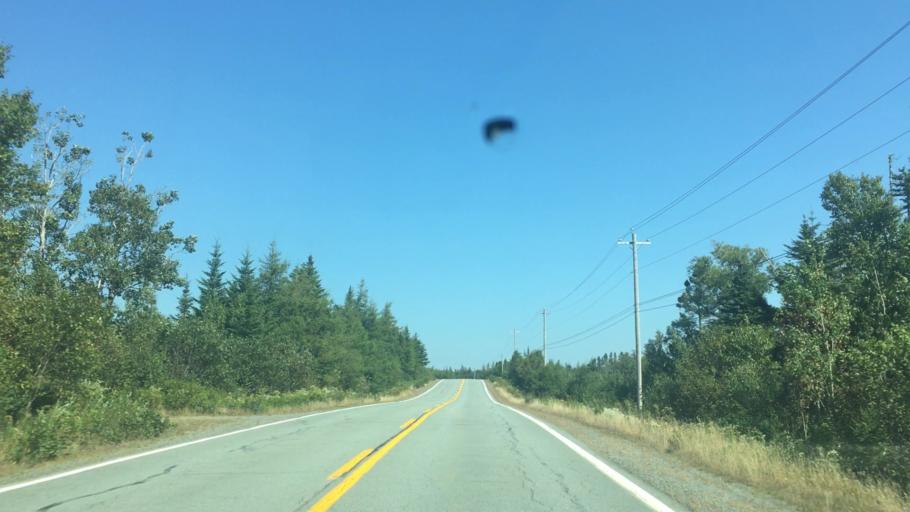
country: CA
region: Nova Scotia
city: Antigonish
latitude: 45.0188
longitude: -62.0331
